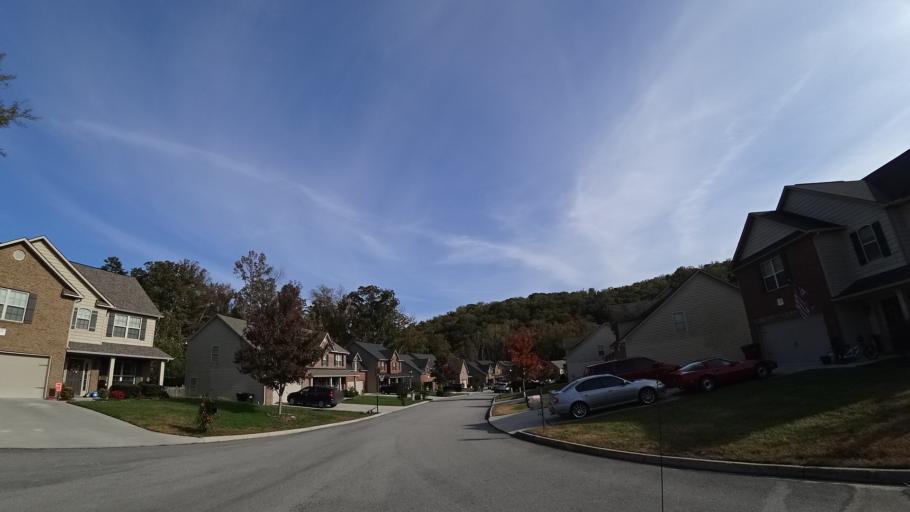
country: US
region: Tennessee
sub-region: Knox County
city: Farragut
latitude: 35.9137
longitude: -84.1824
